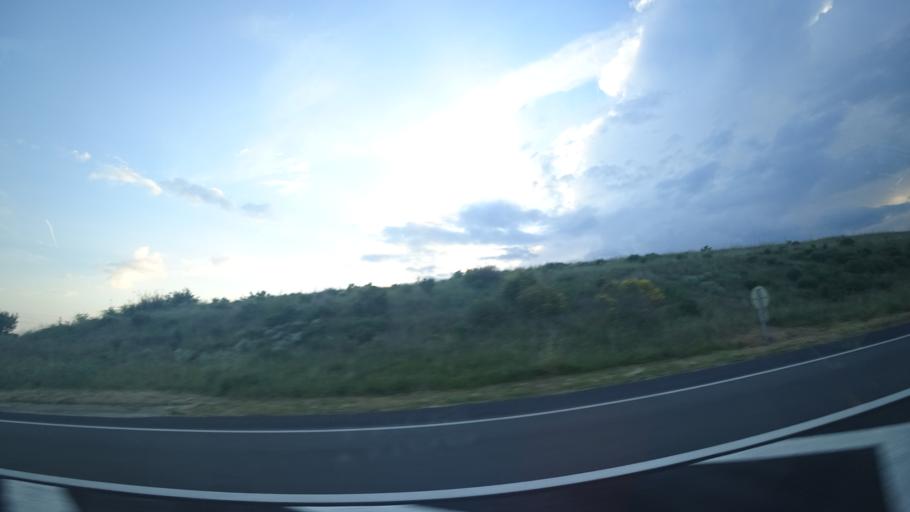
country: FR
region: Languedoc-Roussillon
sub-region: Departement de l'Herault
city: Paulhan
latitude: 43.5271
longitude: 3.4435
